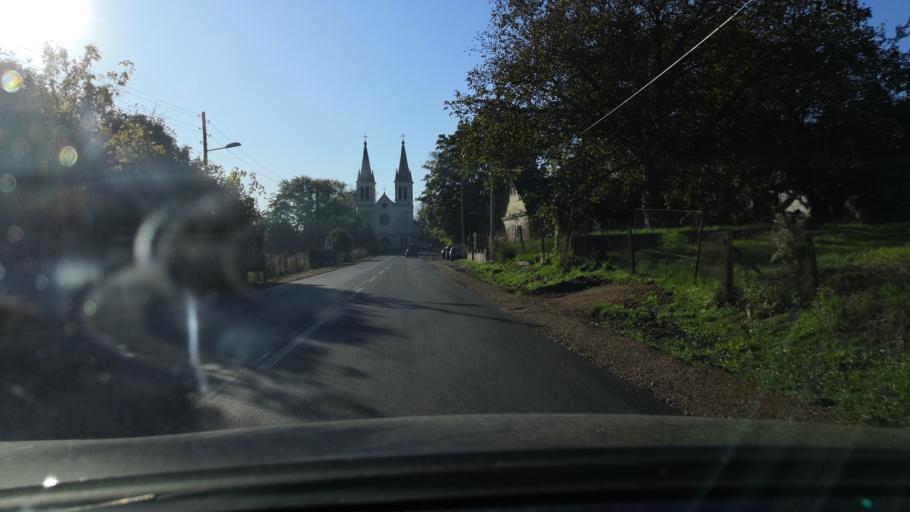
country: RS
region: Autonomna Pokrajina Vojvodina
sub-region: Juznobacki Okrug
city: Petrovaradin
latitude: 45.2295
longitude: 19.8953
